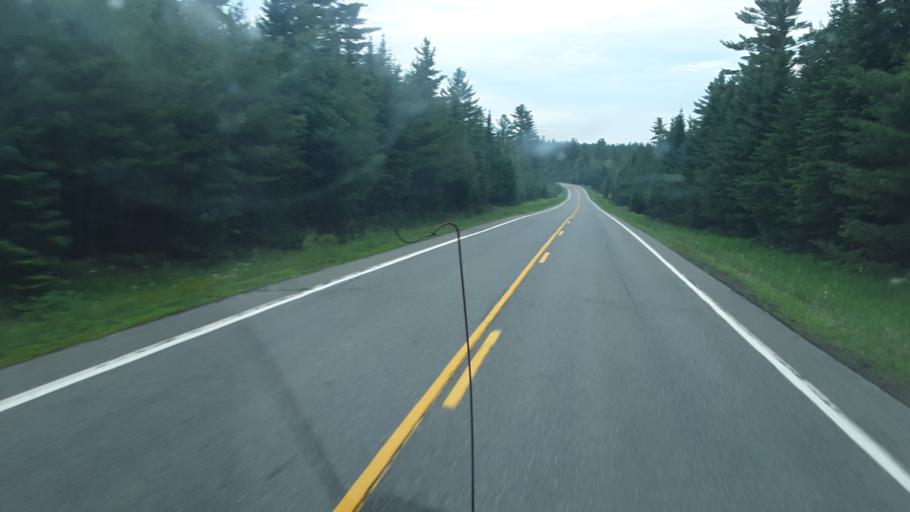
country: US
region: Maine
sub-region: Penobscot County
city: Patten
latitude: 46.4165
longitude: -68.3730
